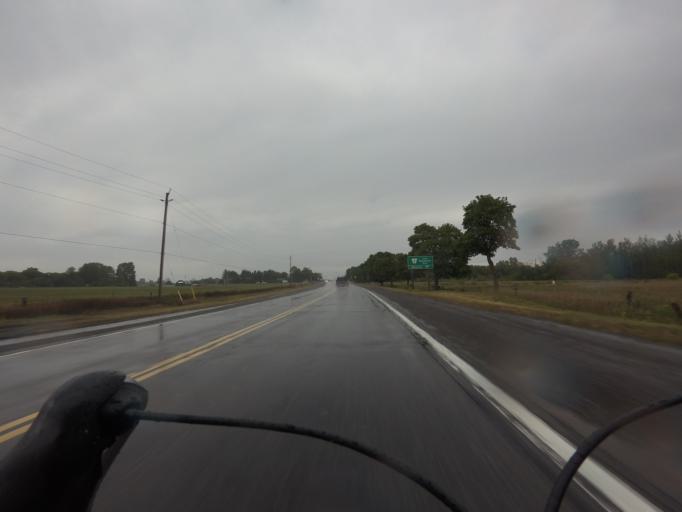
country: CA
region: Ontario
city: Bells Corners
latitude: 45.2151
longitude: -75.7147
